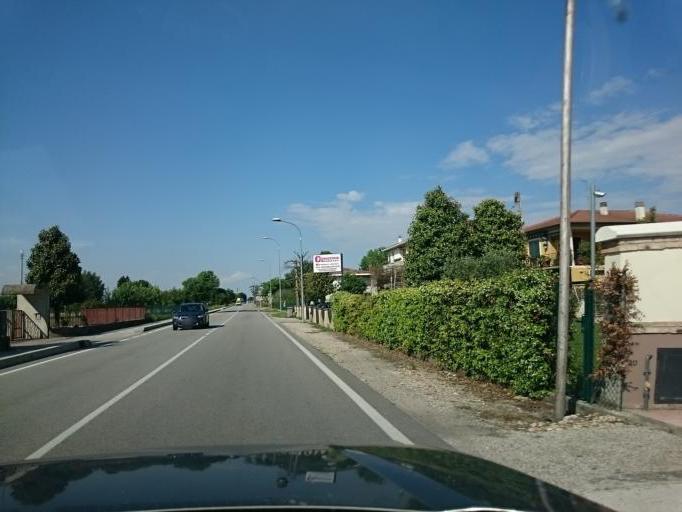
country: IT
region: Veneto
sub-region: Provincia di Vicenza
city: Montegalda
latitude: 45.4518
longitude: 11.6842
